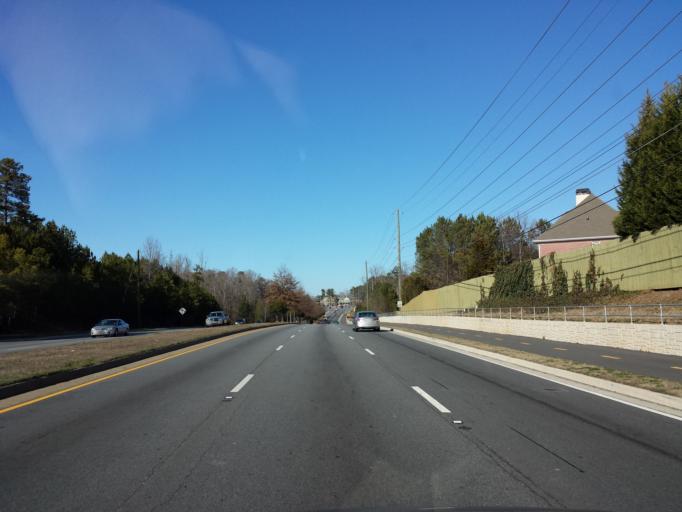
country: US
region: Georgia
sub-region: Cobb County
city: Kennesaw
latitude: 33.9664
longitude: -84.6142
